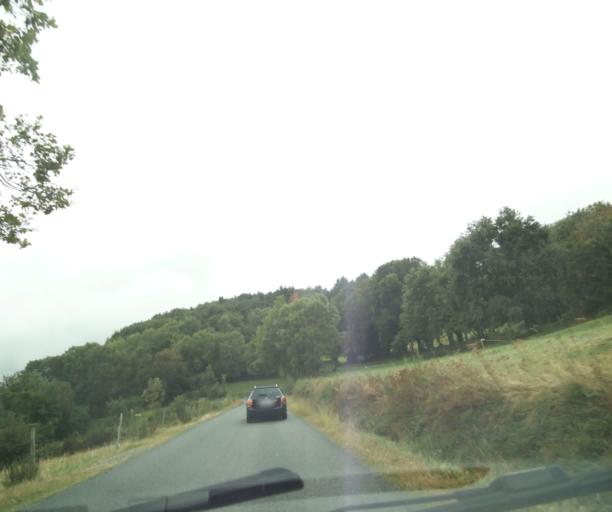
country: FR
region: Auvergne
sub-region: Departement du Puy-de-Dome
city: Orcines
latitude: 45.8019
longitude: 3.0281
